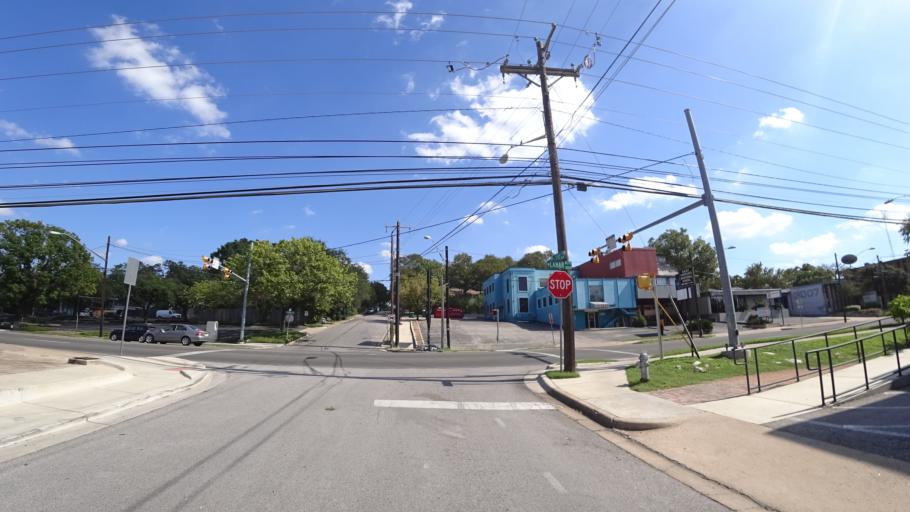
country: US
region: Texas
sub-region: Travis County
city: Austin
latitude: 30.3003
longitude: -97.7465
